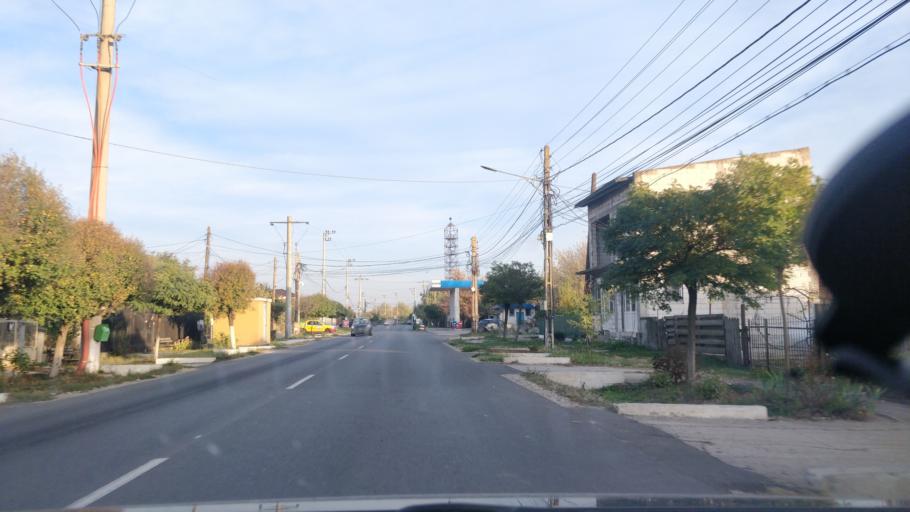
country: RO
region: Ilfov
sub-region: Comuna Ciorogarla
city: Ciorogarla
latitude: 44.4426
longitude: 25.8953
